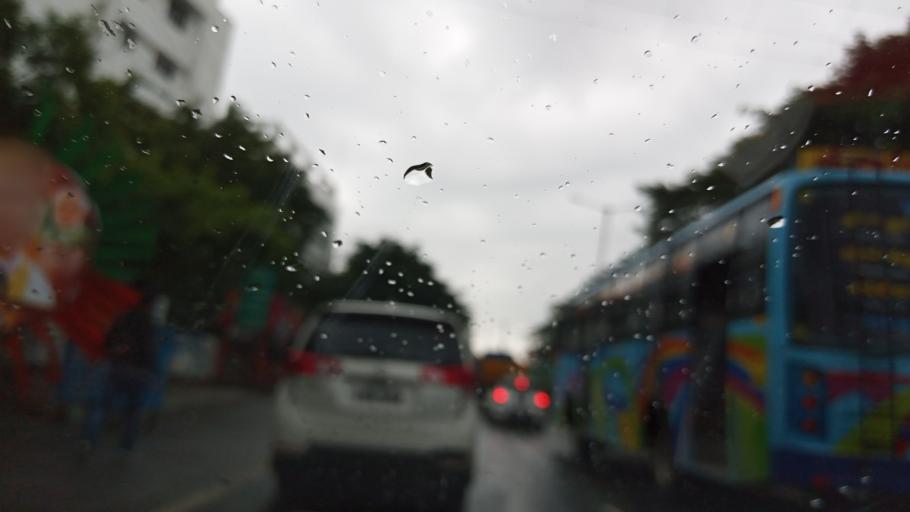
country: IN
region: Pondicherry
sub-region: Puducherry
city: Puducherry
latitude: 11.9329
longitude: 79.8076
